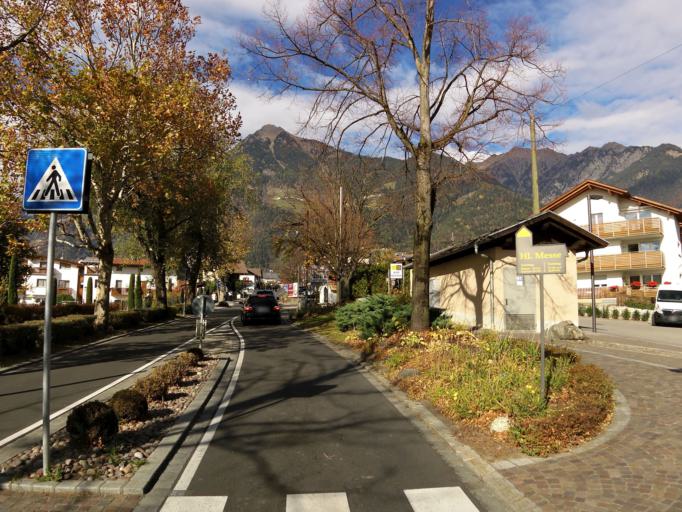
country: IT
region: Trentino-Alto Adige
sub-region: Bolzano
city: Tirolo
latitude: 46.6857
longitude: 11.1592
